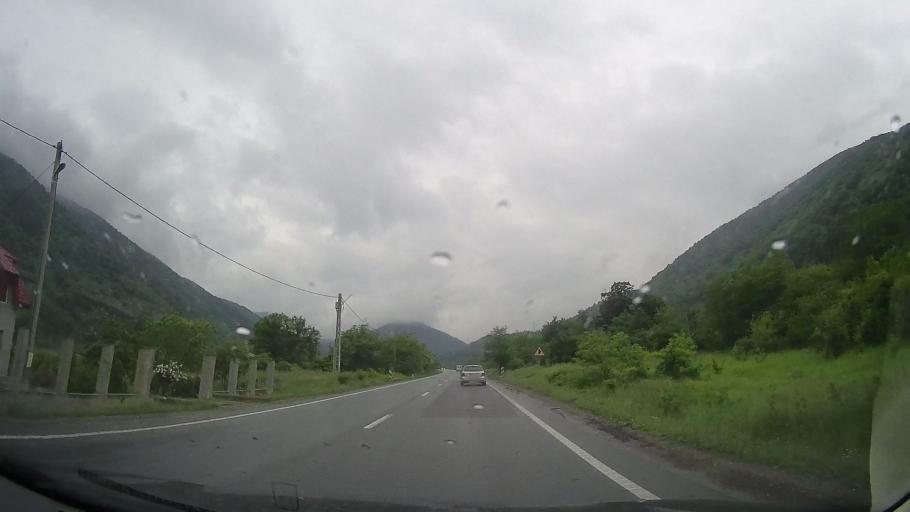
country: RO
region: Caras-Severin
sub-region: Comuna Mehadia
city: Mehadia
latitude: 44.8802
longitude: 22.3838
